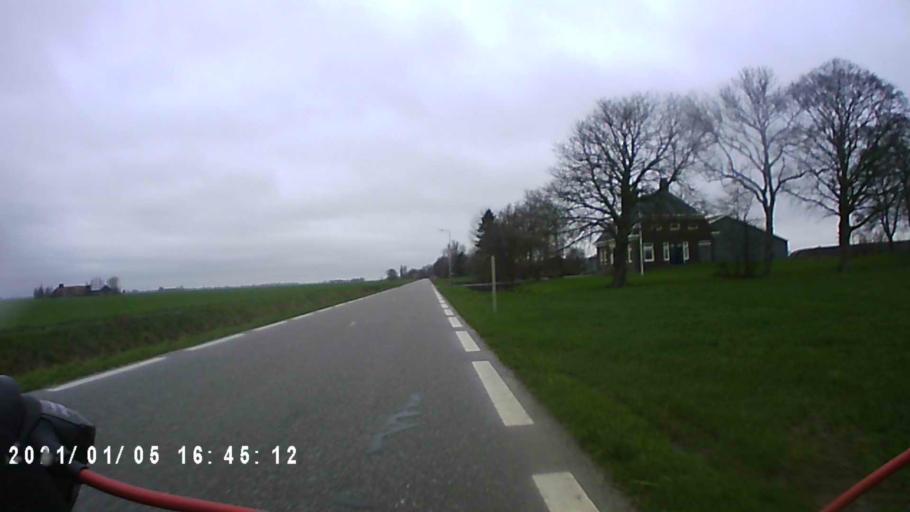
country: NL
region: Groningen
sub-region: Gemeente  Oldambt
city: Winschoten
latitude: 53.2199
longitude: 7.0522
